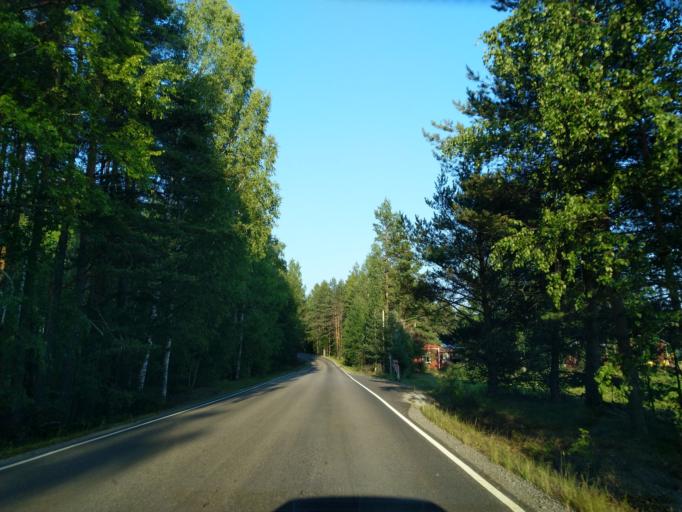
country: FI
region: Satakunta
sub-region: Pohjois-Satakunta
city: Honkajoki
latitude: 61.8200
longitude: 22.2215
